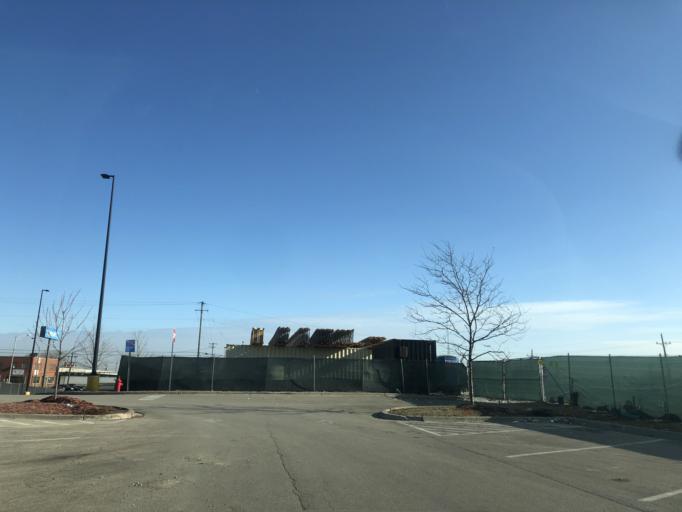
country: US
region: Illinois
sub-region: Cook County
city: Cicero
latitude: 41.8301
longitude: -87.7452
